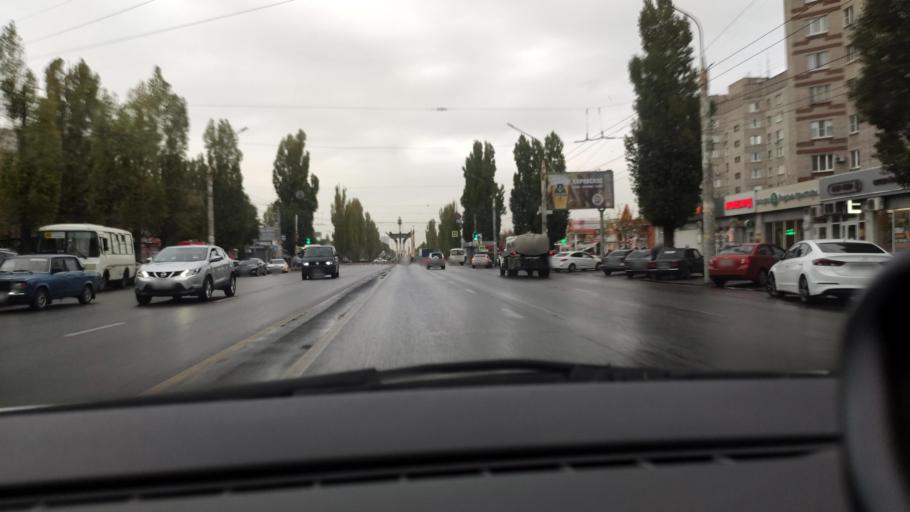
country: RU
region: Voronezj
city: Voronezh
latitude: 51.6828
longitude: 39.2622
